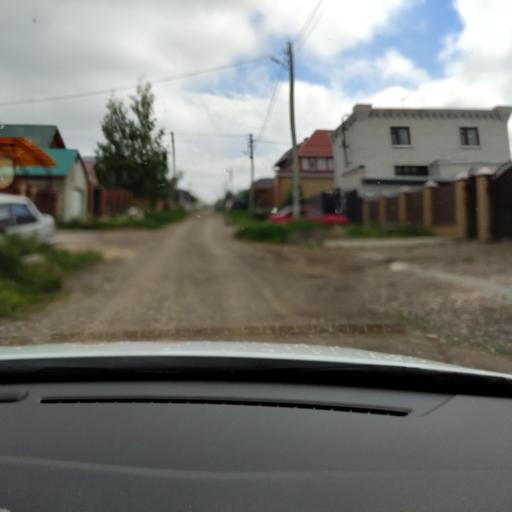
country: RU
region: Tatarstan
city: Stolbishchi
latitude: 55.7762
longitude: 49.2588
